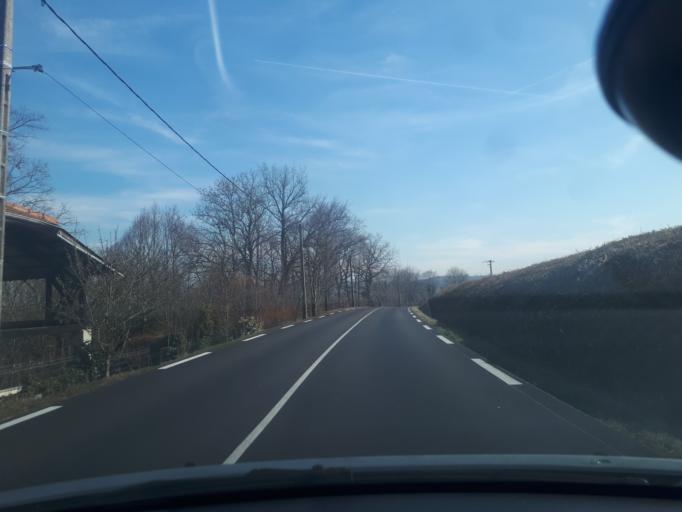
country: FR
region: Rhone-Alpes
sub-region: Departement de l'Isere
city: Salagnon
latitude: 45.6691
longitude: 5.3540
